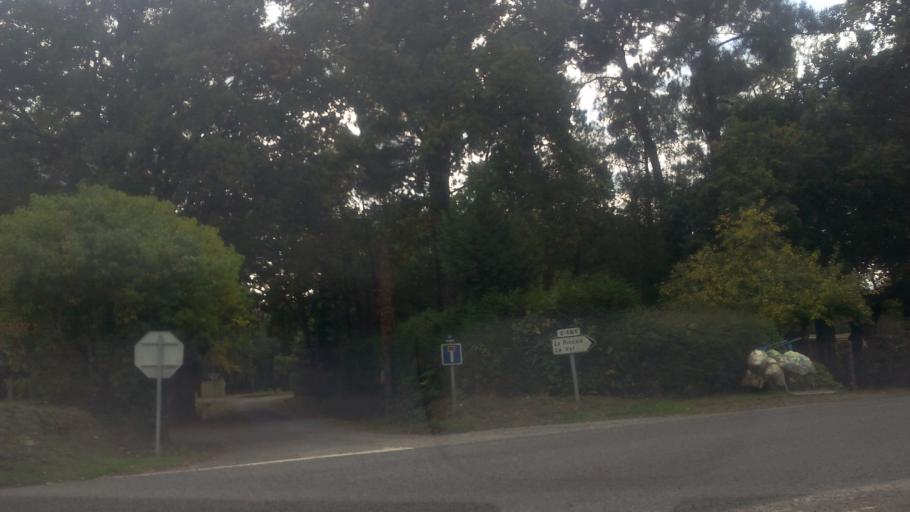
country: FR
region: Brittany
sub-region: Departement du Morbihan
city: Saint-Perreux
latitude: 47.6685
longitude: -2.1208
